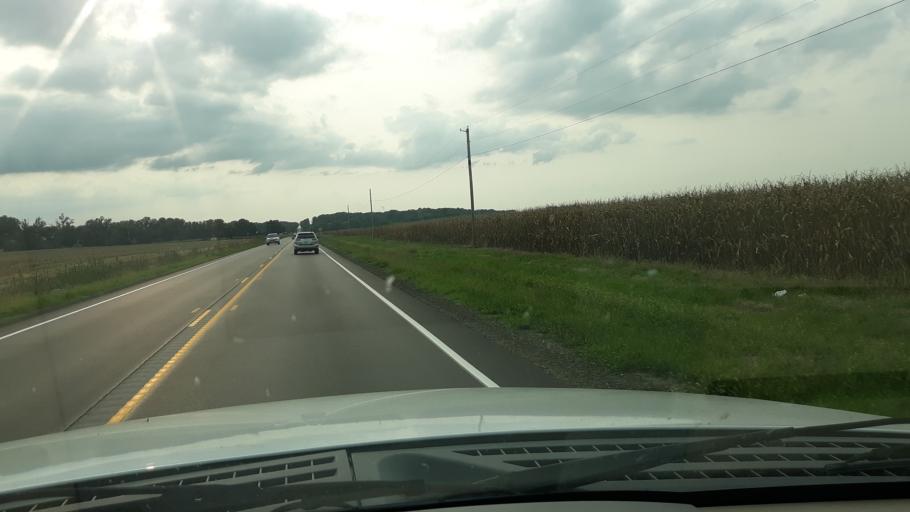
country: US
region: Indiana
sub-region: Gibson County
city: Princeton
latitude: 38.3557
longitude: -87.6339
